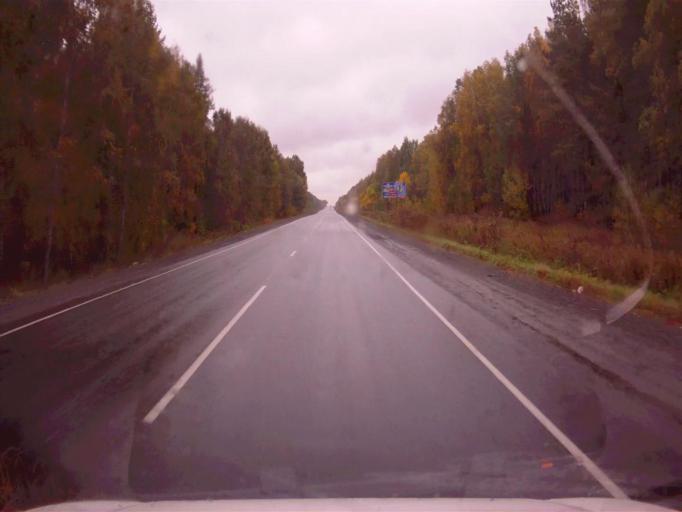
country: RU
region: Chelyabinsk
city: Roshchino
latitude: 55.3730
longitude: 61.1554
